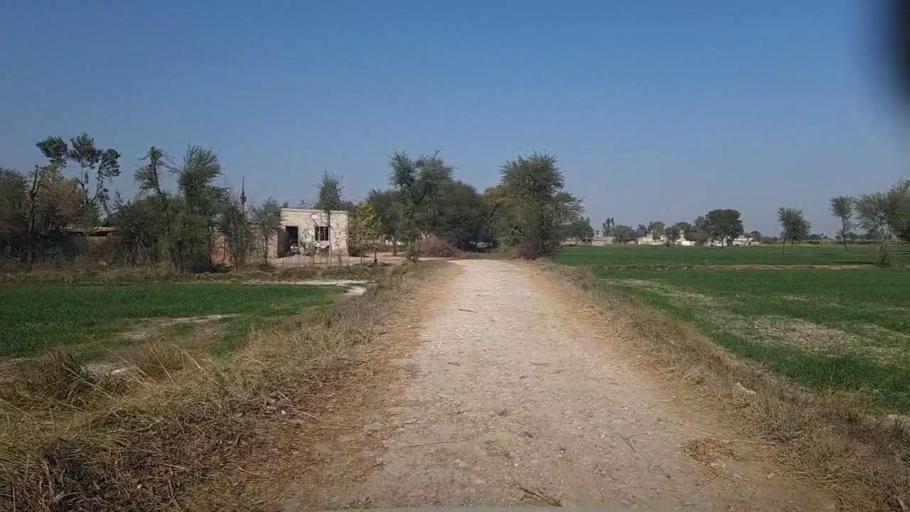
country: PK
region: Sindh
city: Khairpur
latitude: 28.0567
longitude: 69.6726
